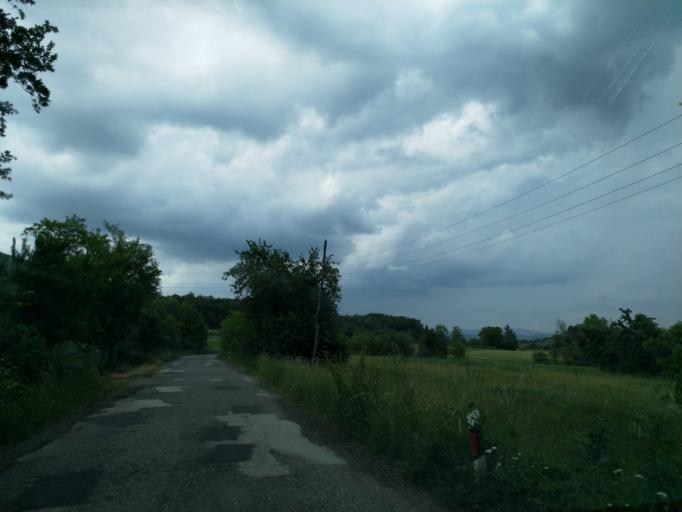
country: RS
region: Central Serbia
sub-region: Zajecarski Okrug
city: Boljevac
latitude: 43.9700
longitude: 21.9696
